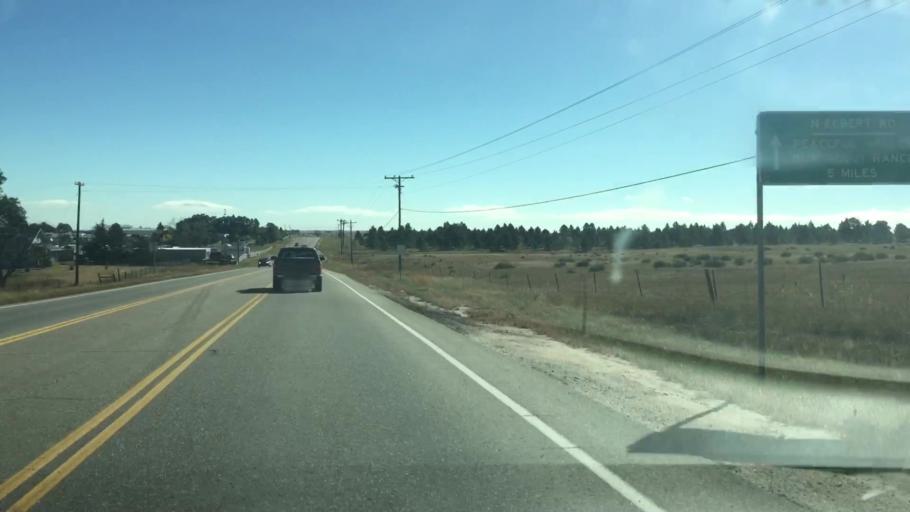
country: US
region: Colorado
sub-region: Elbert County
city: Elizabeth
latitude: 39.3613
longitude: -104.5698
